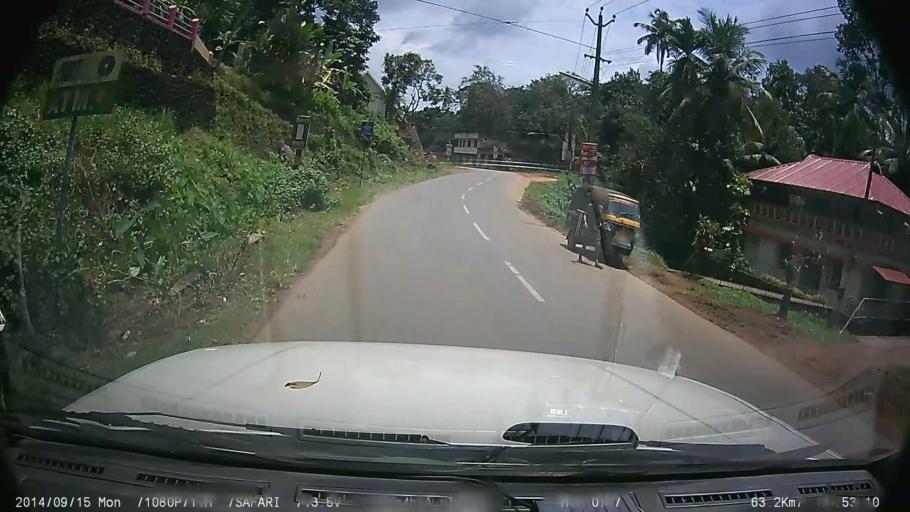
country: IN
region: Kerala
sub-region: Kottayam
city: Palackattumala
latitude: 9.8026
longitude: 76.5748
